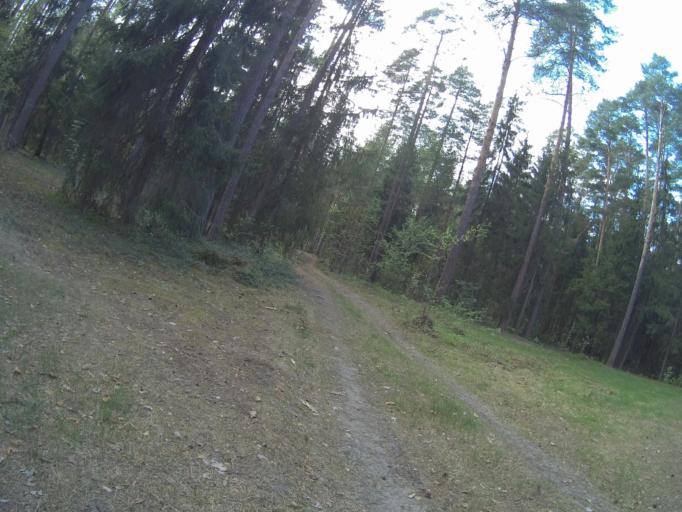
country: RU
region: Vladimir
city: Orgtrud
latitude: 56.1259
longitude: 40.7356
